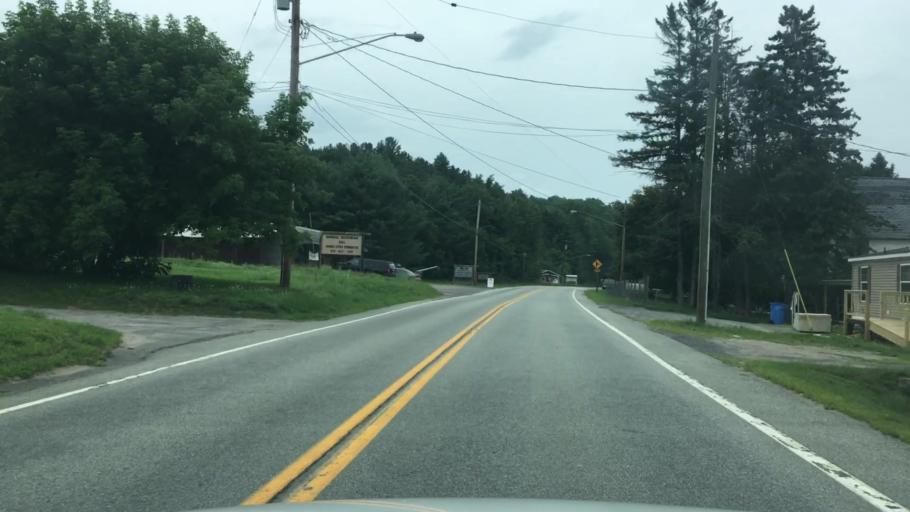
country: US
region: New York
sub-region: Clinton County
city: Peru
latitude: 44.4320
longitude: -73.6811
